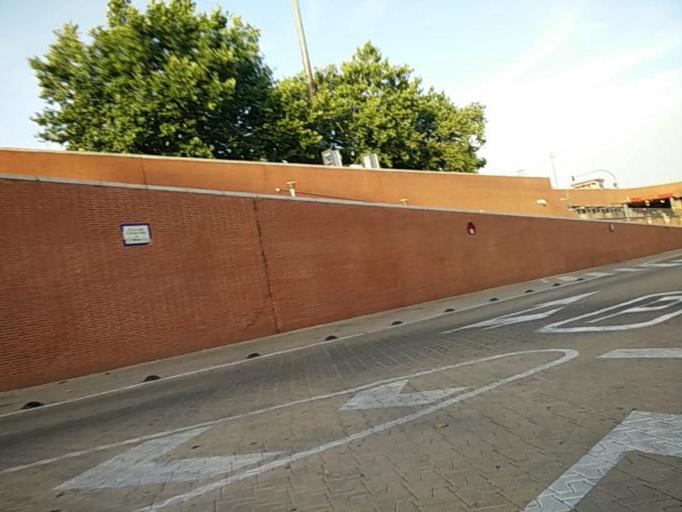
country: ES
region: Madrid
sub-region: Provincia de Madrid
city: Arganzuela
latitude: 40.4075
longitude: -3.6909
